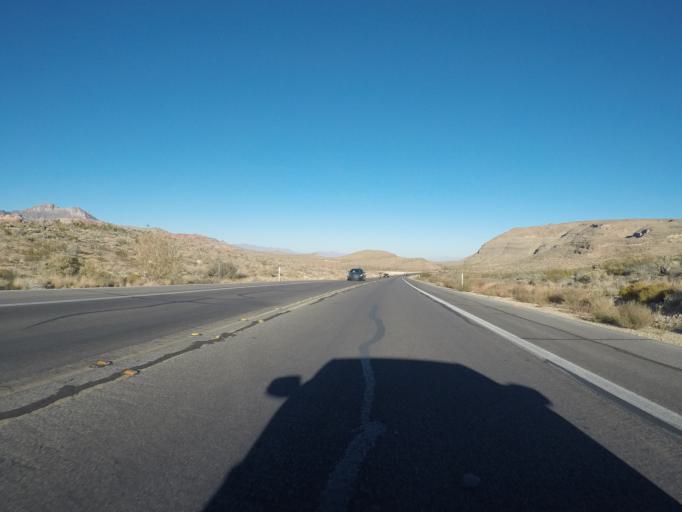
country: US
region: Nevada
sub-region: Clark County
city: Summerlin South
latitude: 36.1176
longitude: -115.4432
